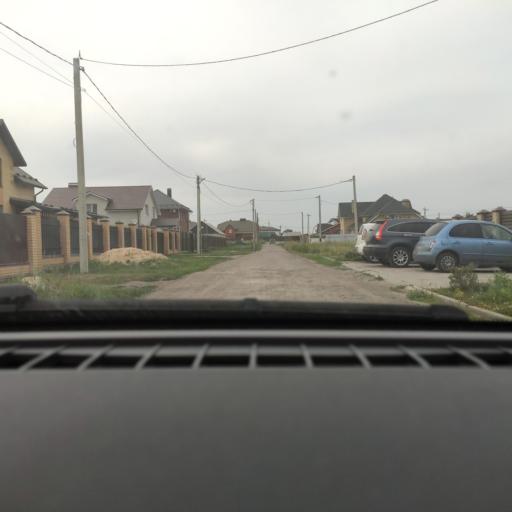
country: RU
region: Voronezj
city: Novaya Usman'
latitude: 51.6481
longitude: 39.3395
